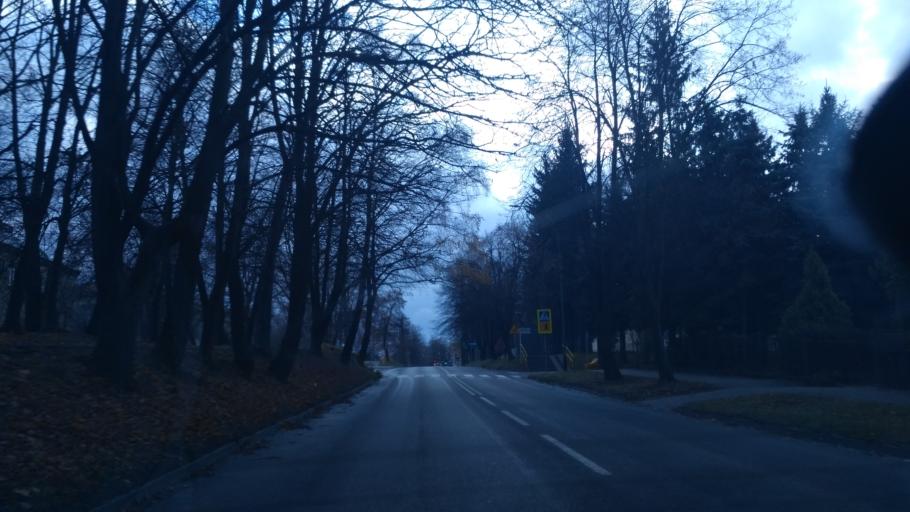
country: PL
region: Subcarpathian Voivodeship
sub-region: Powiat lancucki
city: Lancut
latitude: 50.0728
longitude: 22.2371
